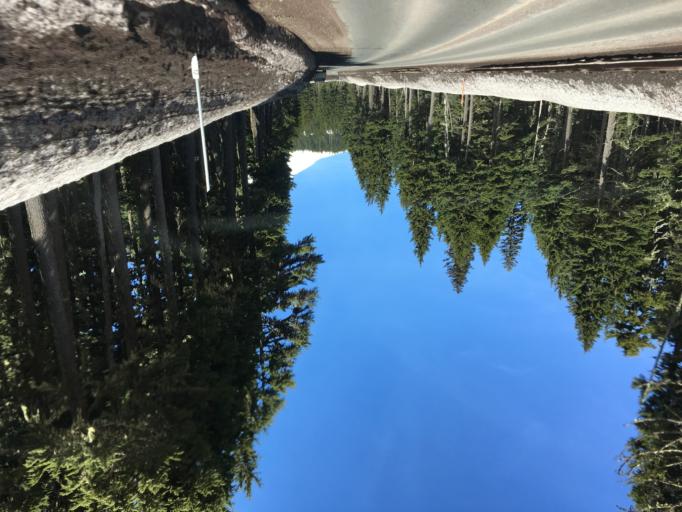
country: US
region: Oregon
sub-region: Clackamas County
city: Mount Hood Village
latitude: 45.3166
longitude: -121.7088
